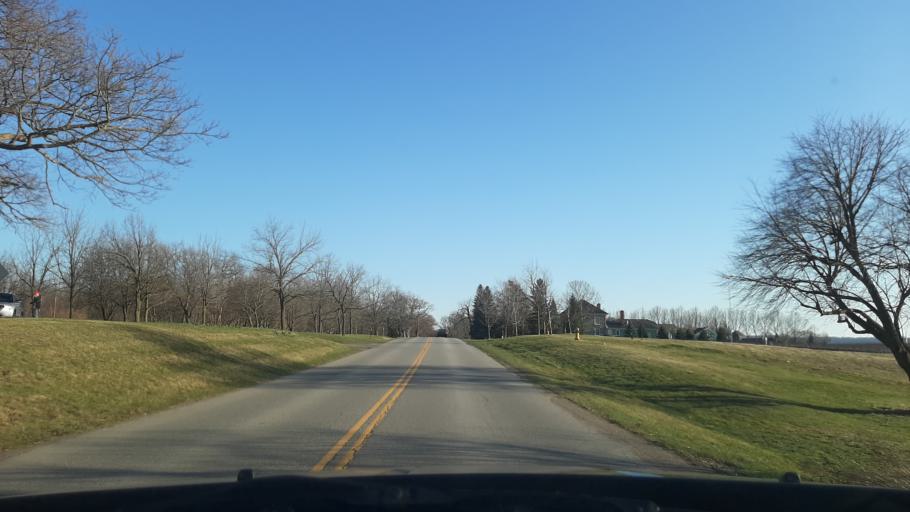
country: US
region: New York
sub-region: Niagara County
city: Lewiston
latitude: 43.1999
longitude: -79.0559
